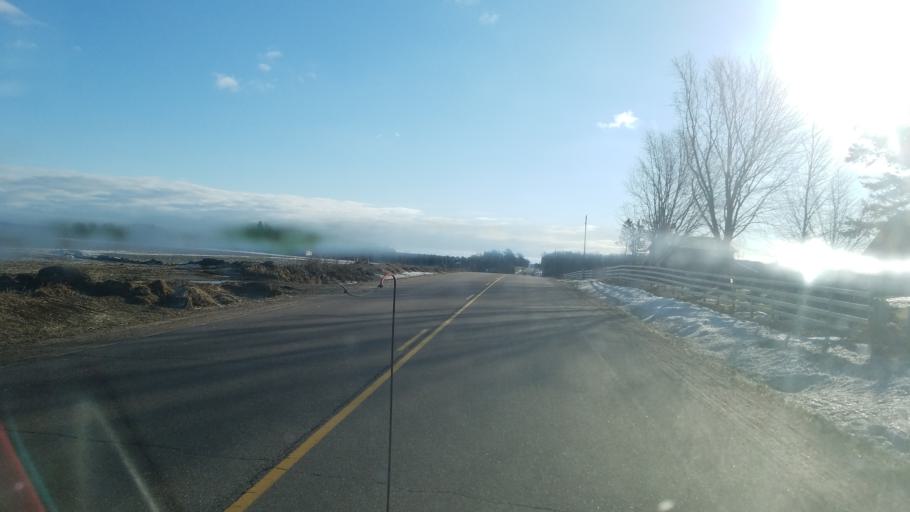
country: US
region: Wisconsin
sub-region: Clark County
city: Loyal
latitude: 44.6542
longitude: -90.4034
